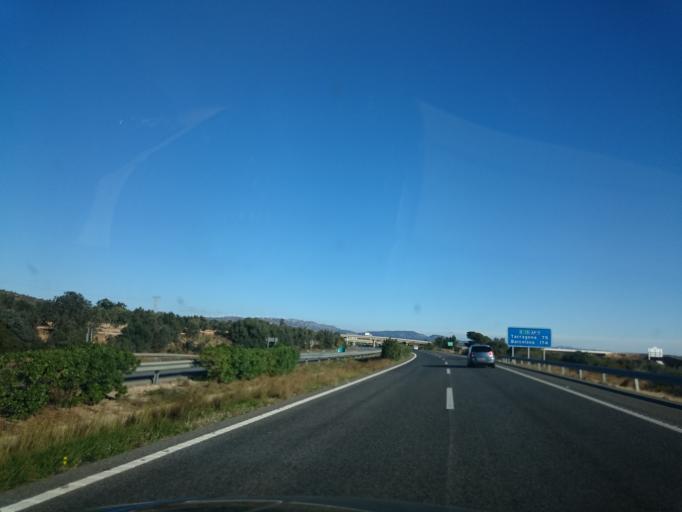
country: ES
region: Catalonia
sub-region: Provincia de Tarragona
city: Amposta
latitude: 40.7363
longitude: 0.5900
